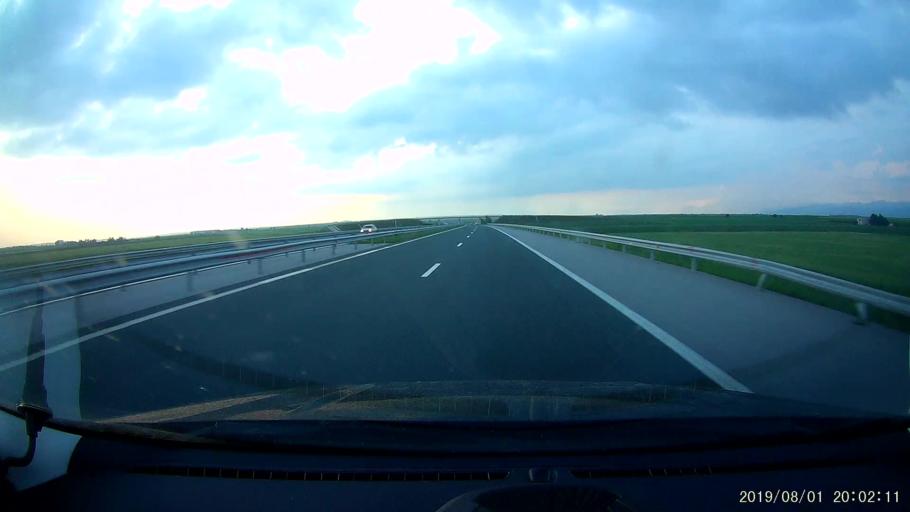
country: BG
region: Yambol
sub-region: Obshtina Straldzha
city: Straldzha
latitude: 42.5588
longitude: 26.6386
